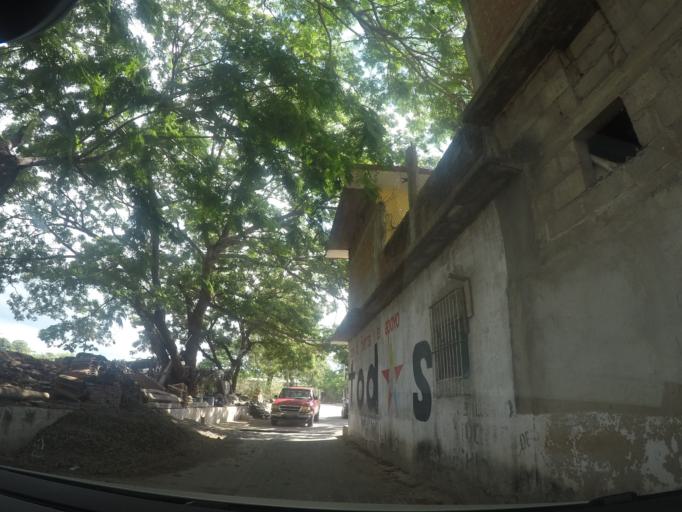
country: MX
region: Oaxaca
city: Juchitan de Zaragoza
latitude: 16.4303
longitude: -95.0256
